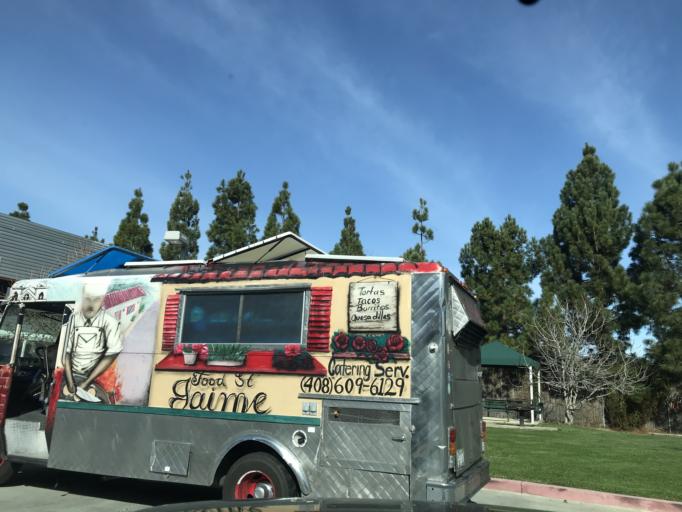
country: US
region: California
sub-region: San Mateo County
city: East Palo Alto
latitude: 37.4762
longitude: -122.1514
